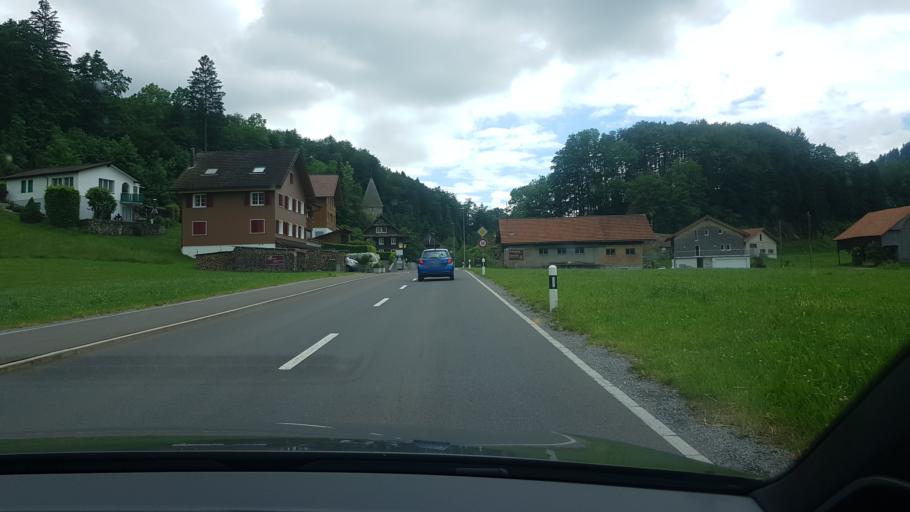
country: CH
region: Schwyz
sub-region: Bezirk Schwyz
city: Sattel
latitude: 47.0934
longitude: 8.6345
